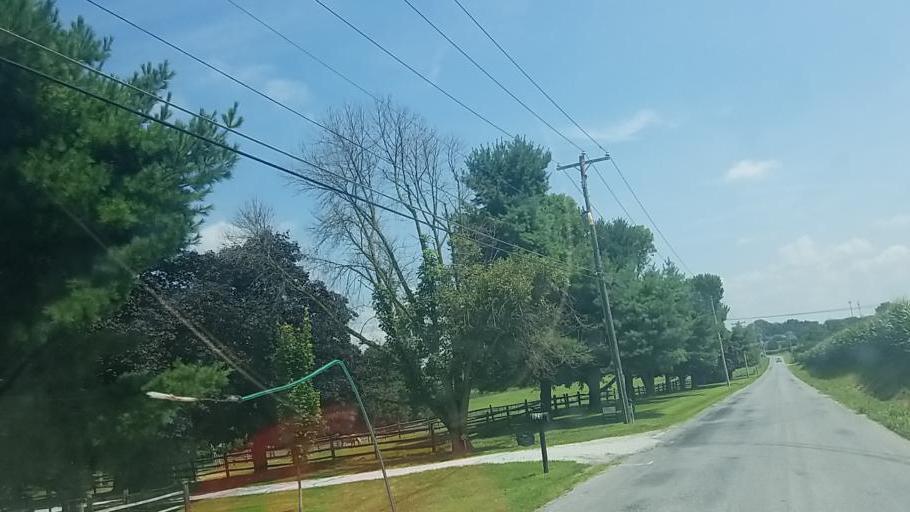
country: US
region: Pennsylvania
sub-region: Chester County
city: Atglen
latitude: 39.8897
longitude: -75.9368
